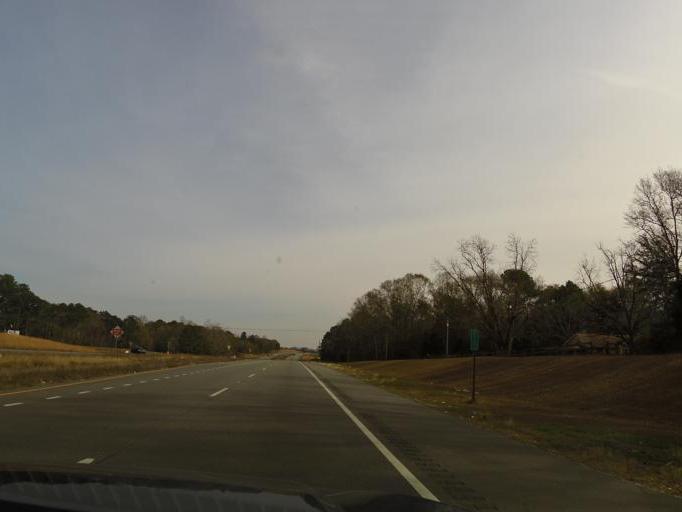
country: US
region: Alabama
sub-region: Houston County
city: Ashford
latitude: 31.1863
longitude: -85.2692
